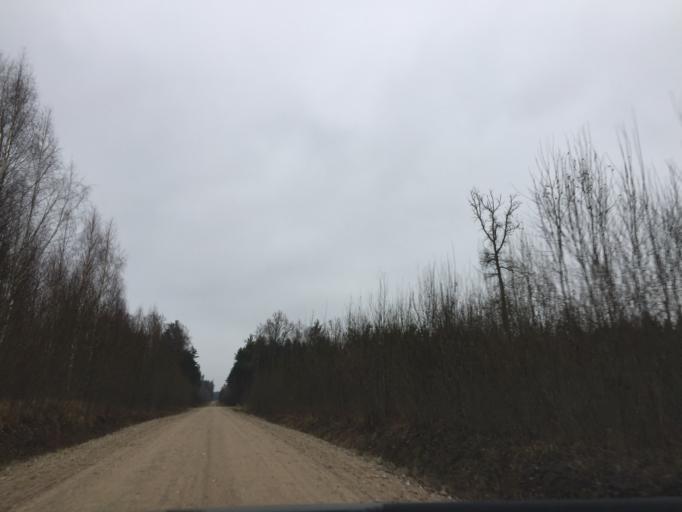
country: LV
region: Limbazu Rajons
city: Limbazi
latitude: 57.4792
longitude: 24.7535
